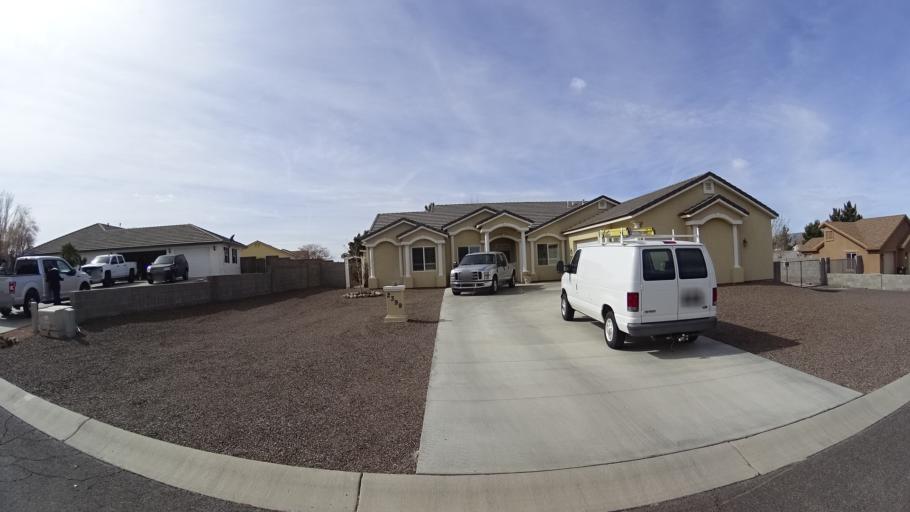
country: US
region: Arizona
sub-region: Mohave County
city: Kingman
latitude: 35.1932
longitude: -113.9770
